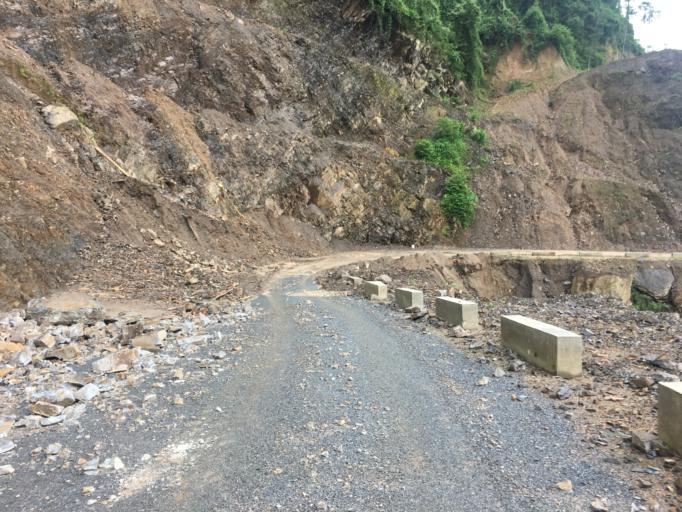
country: VN
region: Ha Giang
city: Thi Tran Tam Son
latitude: 22.9631
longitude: 105.0405
